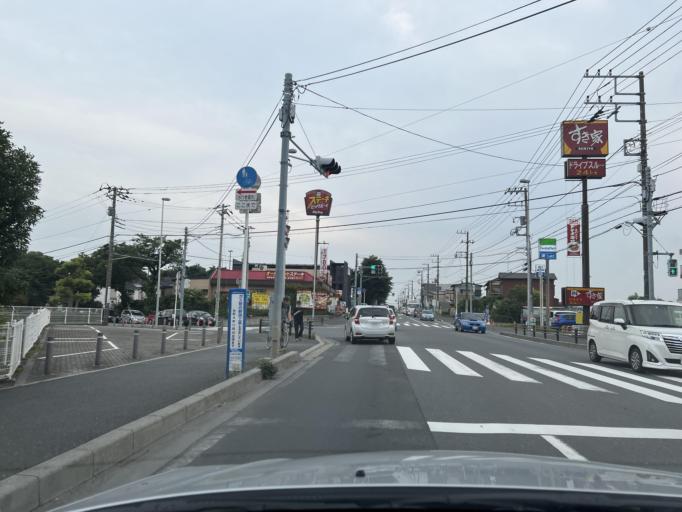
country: JP
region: Chiba
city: Funabashi
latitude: 35.7220
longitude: 139.9589
